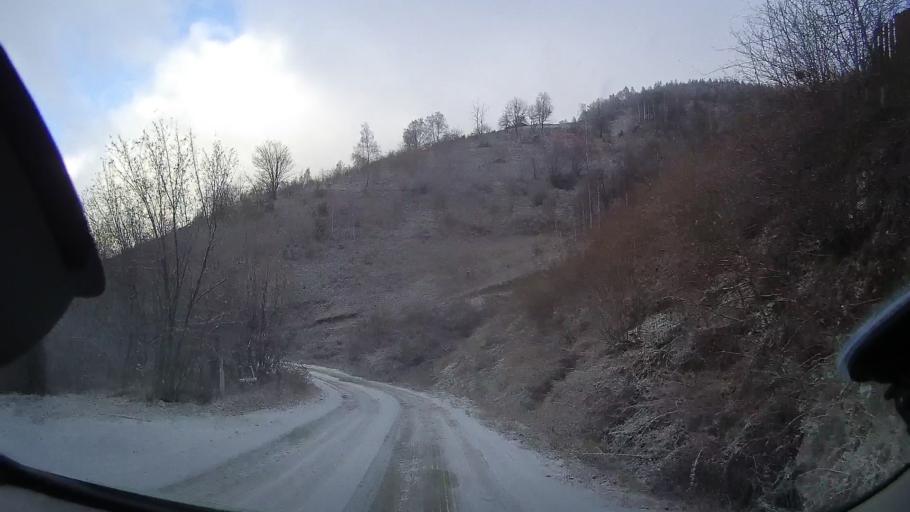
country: RO
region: Cluj
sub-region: Comuna Valea Ierii
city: Valea Ierii
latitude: 46.6692
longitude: 23.3298
